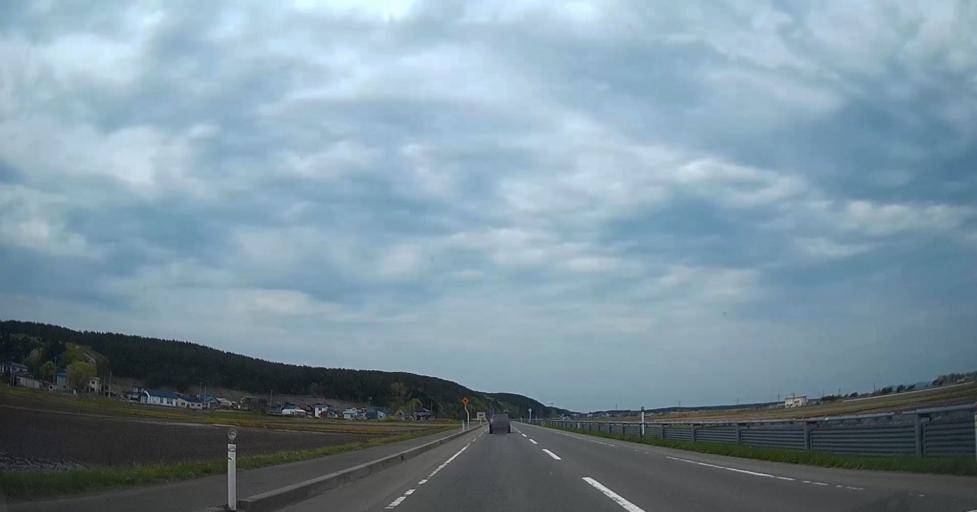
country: JP
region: Aomori
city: Shimokizukuri
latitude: 40.9933
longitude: 140.3603
